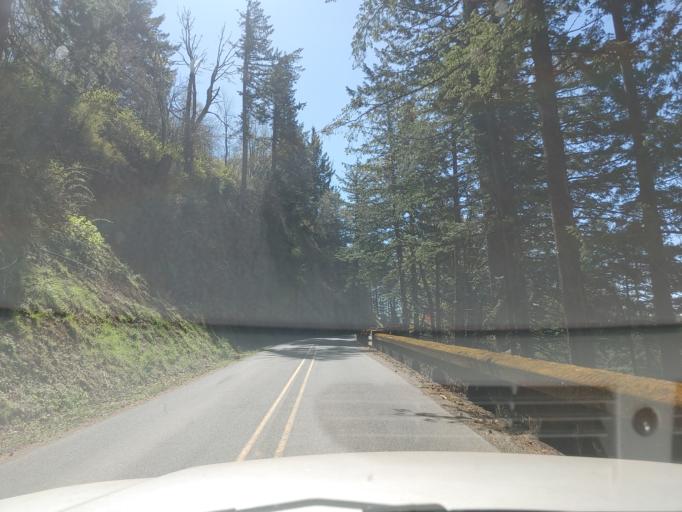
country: US
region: Washington
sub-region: Clark County
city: Washougal
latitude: 45.5361
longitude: -122.2478
